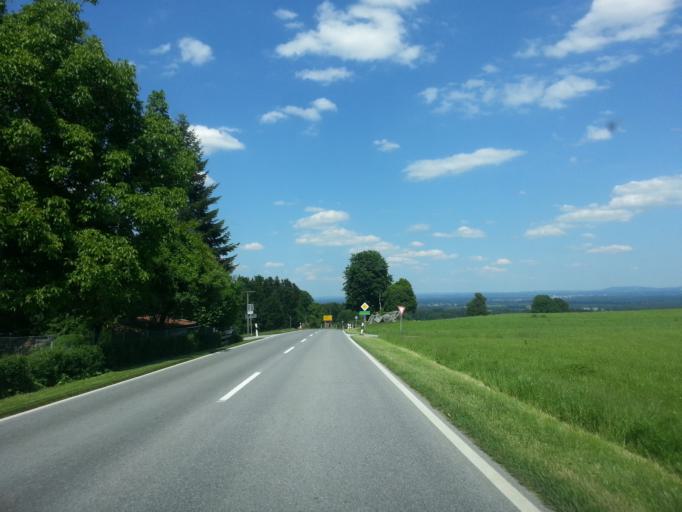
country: DE
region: Bavaria
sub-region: Upper Bavaria
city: Irschenberg
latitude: 47.8088
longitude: 11.9339
